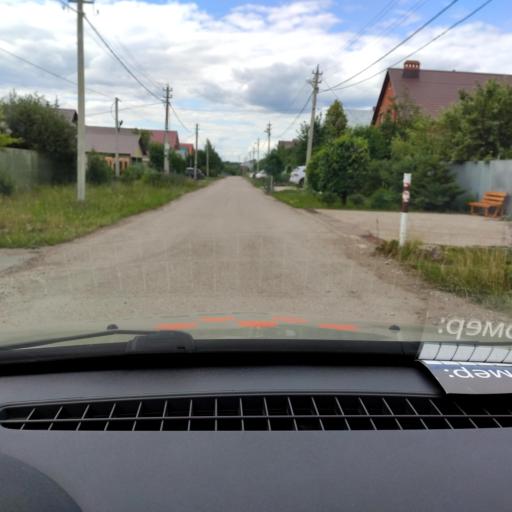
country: RU
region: Bashkortostan
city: Ufa
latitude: 54.6018
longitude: 55.9317
